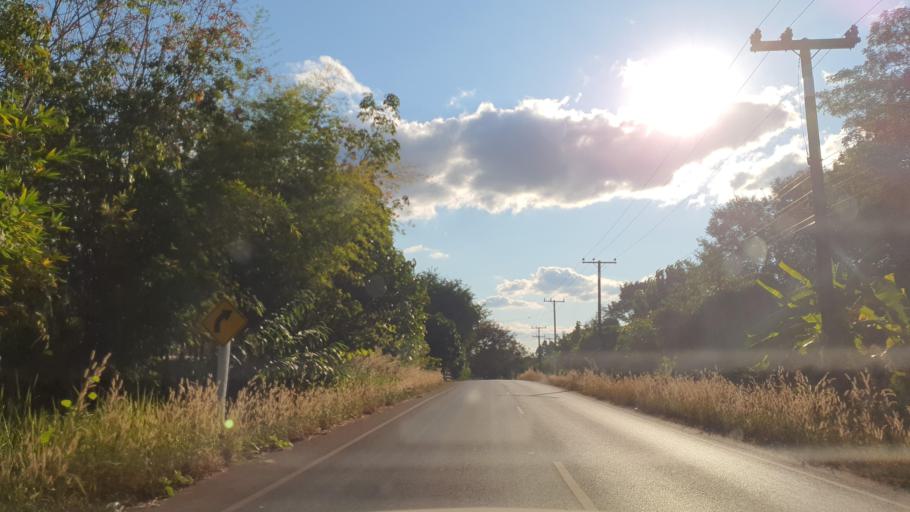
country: TH
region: Changwat Bueng Kan
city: Si Wilai
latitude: 18.1417
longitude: 103.8950
